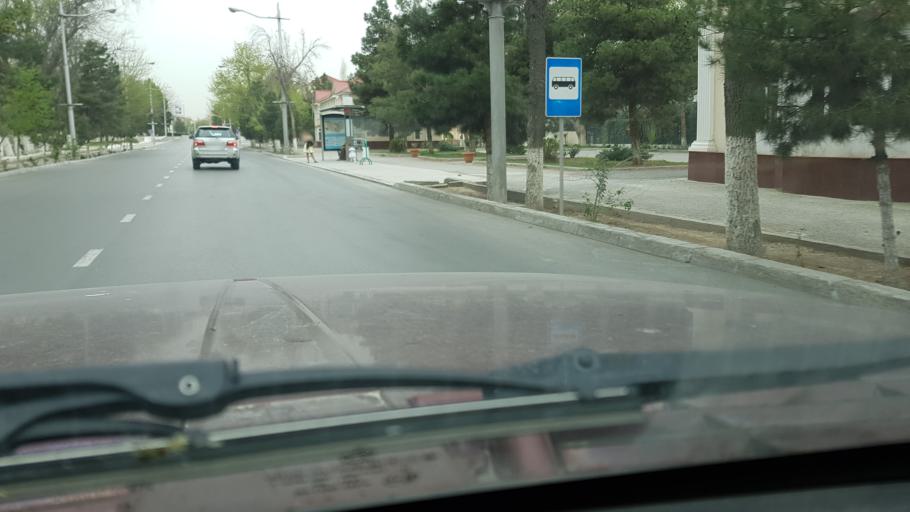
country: TM
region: Ahal
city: Ashgabat
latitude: 37.9462
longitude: 58.3571
